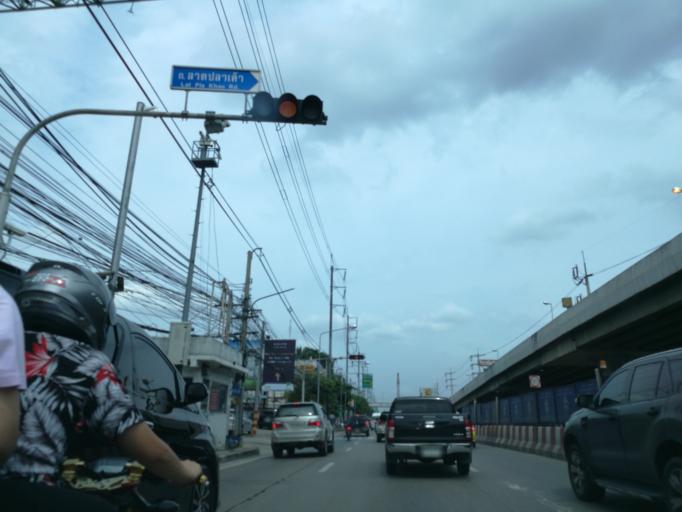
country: TH
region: Bangkok
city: Bang Khen
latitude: 13.8648
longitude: 100.6143
